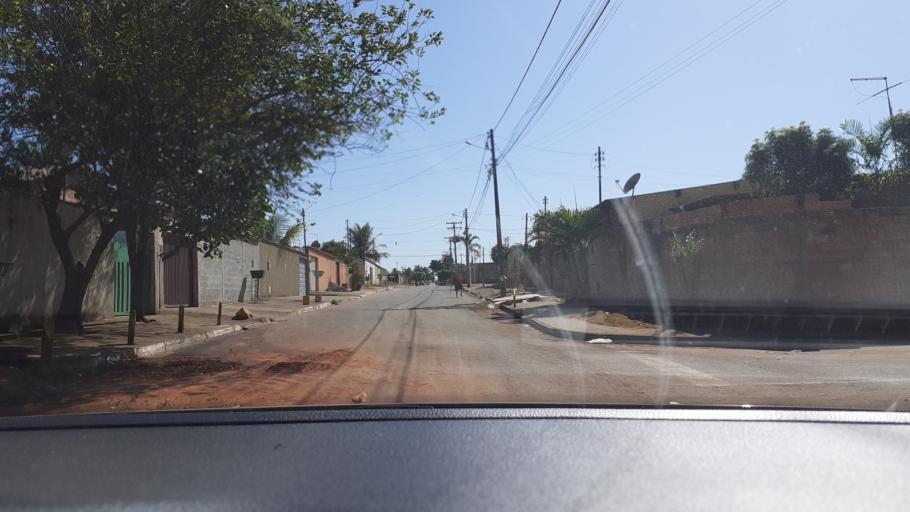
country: BR
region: Goias
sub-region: Aparecida De Goiania
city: Aparecida de Goiania
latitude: -16.8419
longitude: -49.2485
